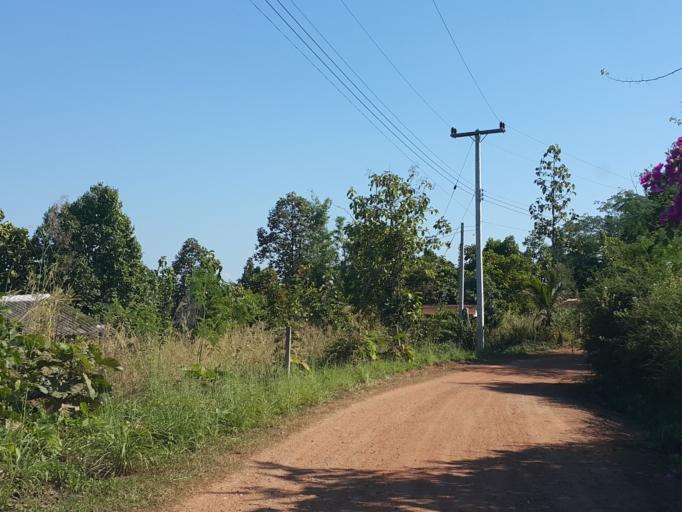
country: TH
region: Chiang Mai
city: Mae Taeng
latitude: 18.9509
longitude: 98.9068
